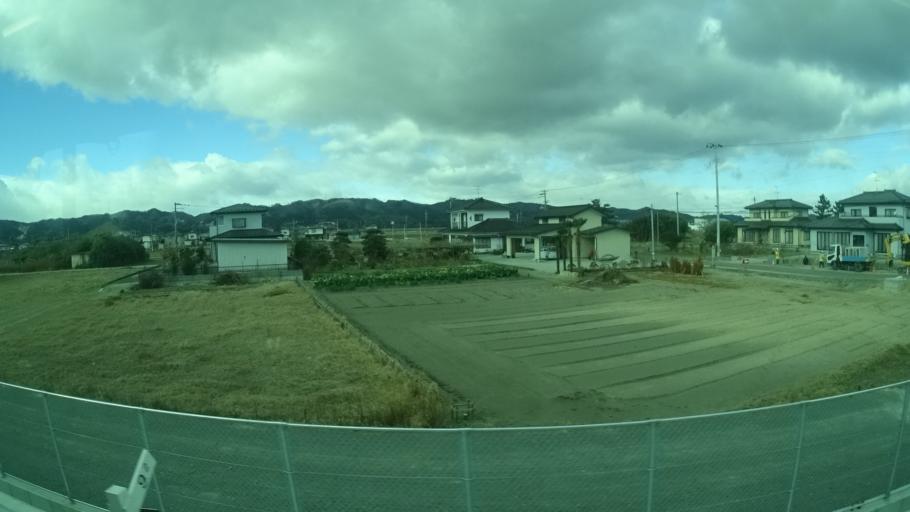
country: JP
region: Miyagi
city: Watari
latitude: 37.9896
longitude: 140.8918
